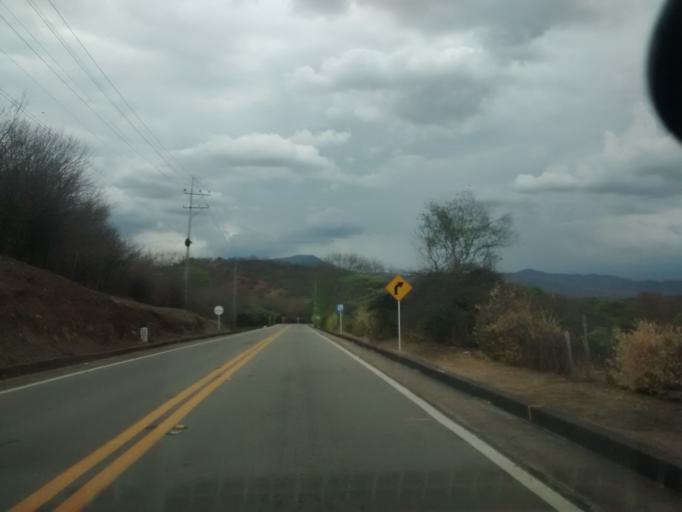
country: CO
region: Cundinamarca
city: Agua de Dios
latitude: 4.4328
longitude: -74.6882
